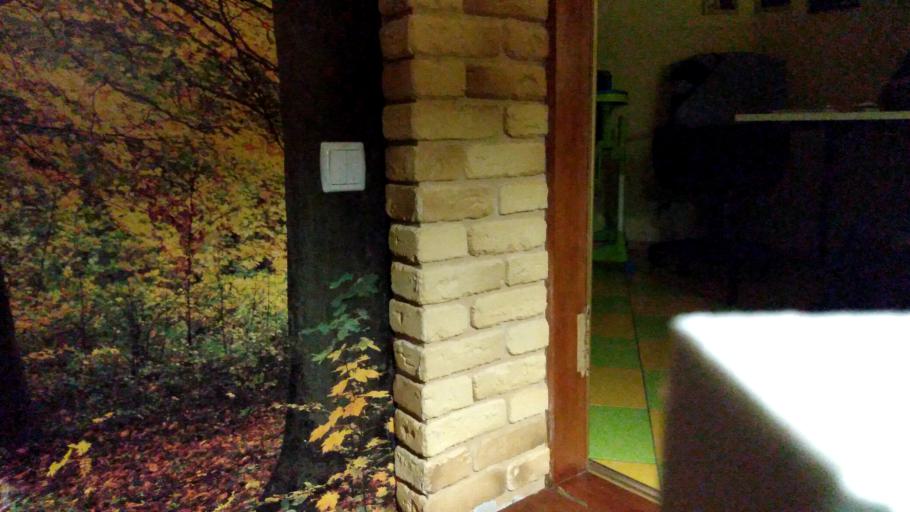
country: RU
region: Vologda
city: Lipin Bor
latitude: 61.0498
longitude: 37.9428
